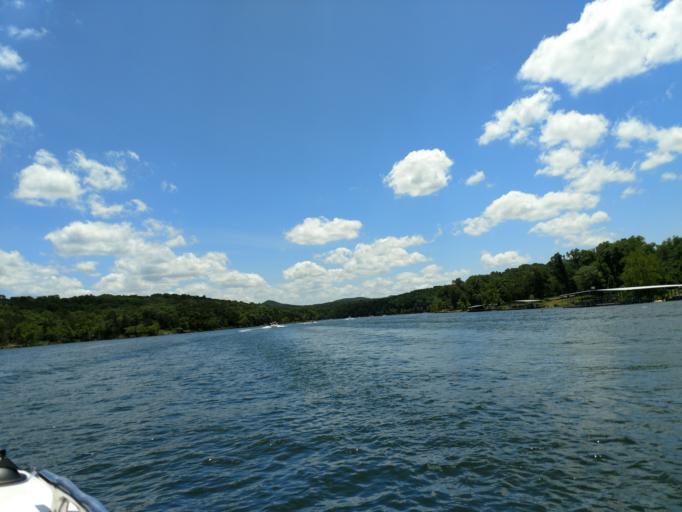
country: US
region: Missouri
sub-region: Barry County
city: Shell Knob
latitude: 36.5801
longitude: -93.5667
